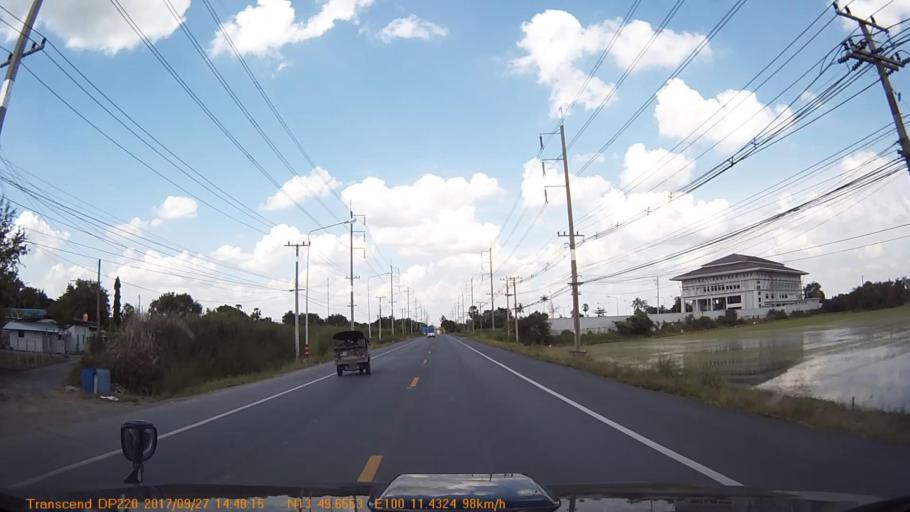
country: TH
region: Nakhon Pathom
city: Nakhon Chai Si
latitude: 13.8278
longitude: 100.1907
